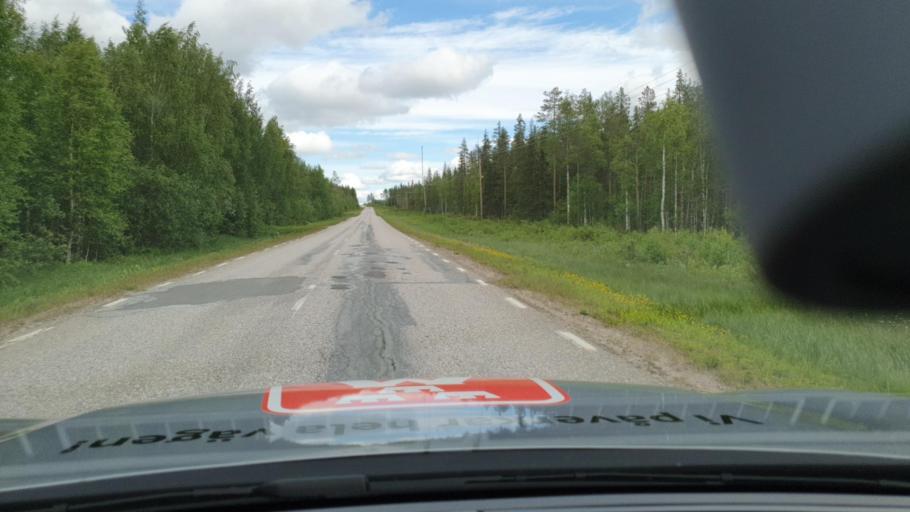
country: SE
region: Norrbotten
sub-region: Kalix Kommun
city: Kalix
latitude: 66.0330
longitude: 23.1699
